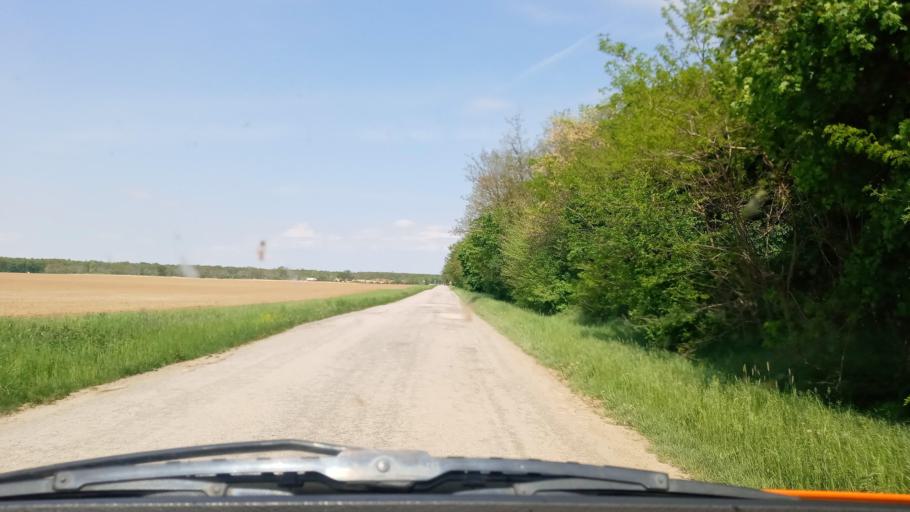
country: HU
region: Baranya
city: Boly
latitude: 45.8822
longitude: 18.5715
